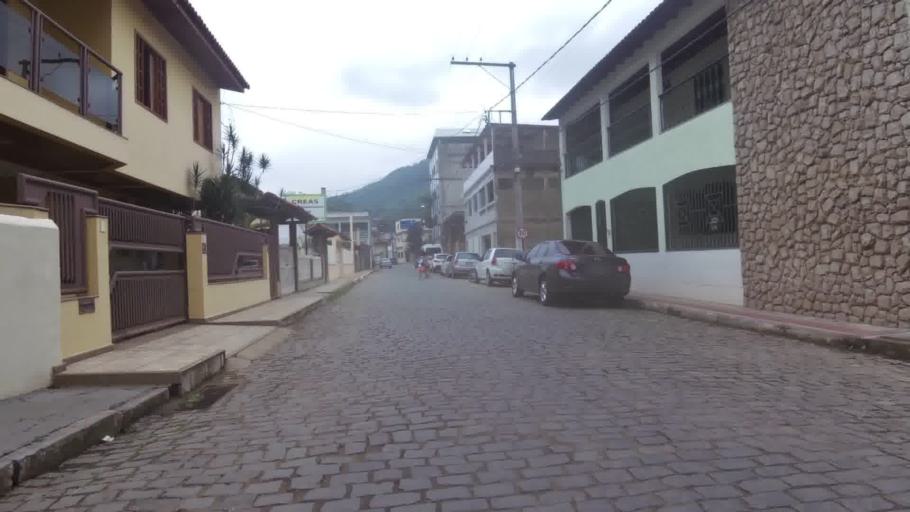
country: BR
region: Espirito Santo
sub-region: Iconha
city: Iconha
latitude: -20.7932
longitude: -40.8125
